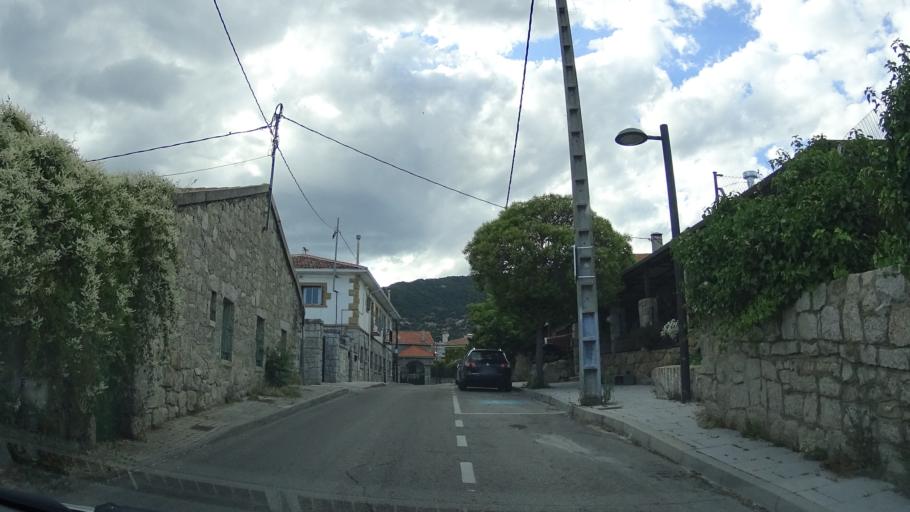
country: ES
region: Madrid
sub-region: Provincia de Madrid
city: Hoyo de Manzanares
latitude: 40.6244
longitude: -3.9030
